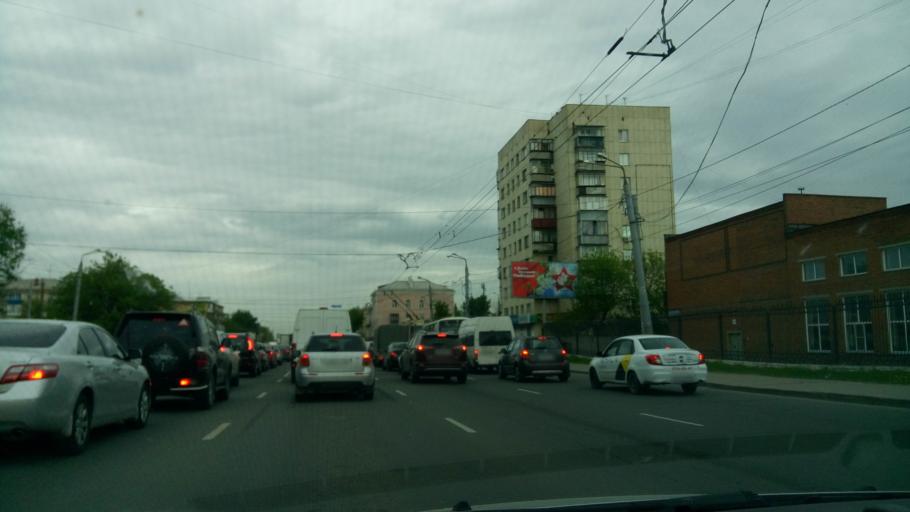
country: RU
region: Chelyabinsk
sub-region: Gorod Chelyabinsk
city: Chelyabinsk
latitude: 55.1826
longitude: 61.3872
